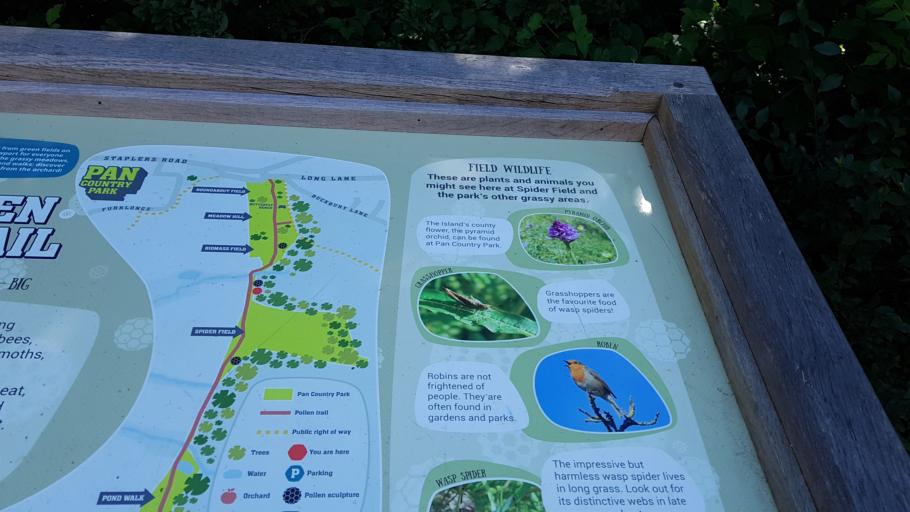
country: GB
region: England
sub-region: Isle of Wight
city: Newport
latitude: 50.6974
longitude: -1.2762
